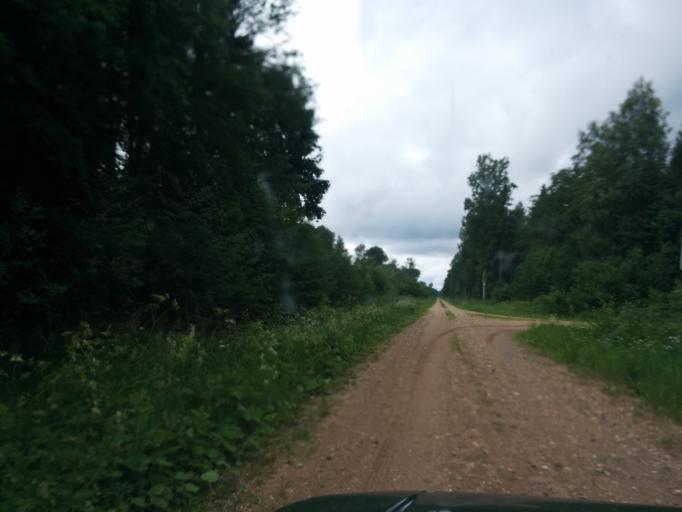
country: LV
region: Vilaka
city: Vilaka
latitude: 57.3916
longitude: 27.5652
